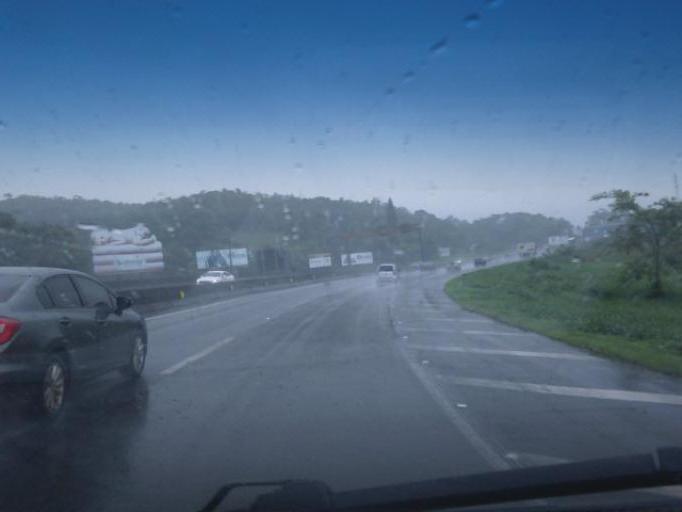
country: BR
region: Santa Catarina
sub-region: Joinville
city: Joinville
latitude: -26.3818
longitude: -48.8516
